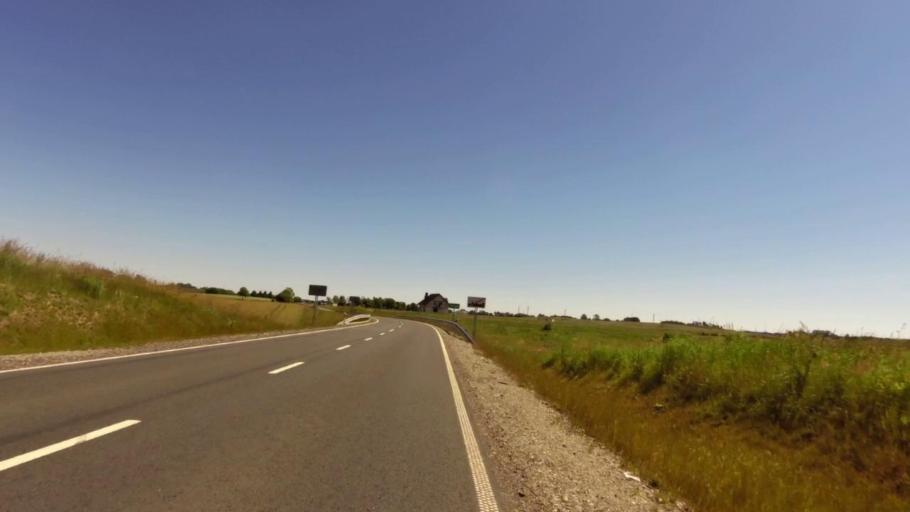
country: PL
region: West Pomeranian Voivodeship
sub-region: Powiat kolobrzeski
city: Goscino
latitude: 54.0446
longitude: 15.6520
